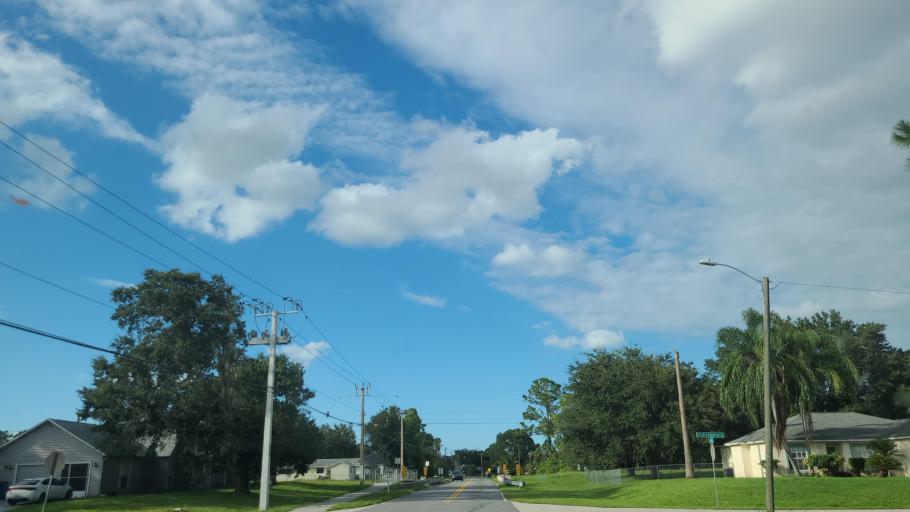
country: US
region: Florida
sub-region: Brevard County
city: West Melbourne
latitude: 28.0054
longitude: -80.6629
